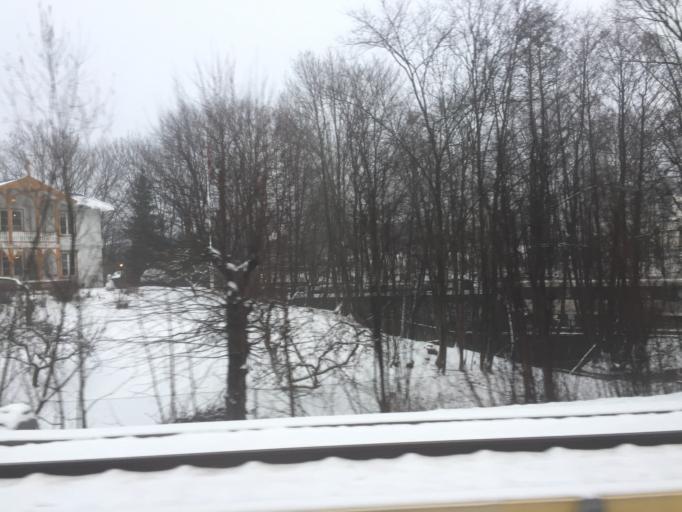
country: NO
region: Oslo
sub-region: Oslo
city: Sjolyststranda
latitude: 59.9357
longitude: 10.7082
